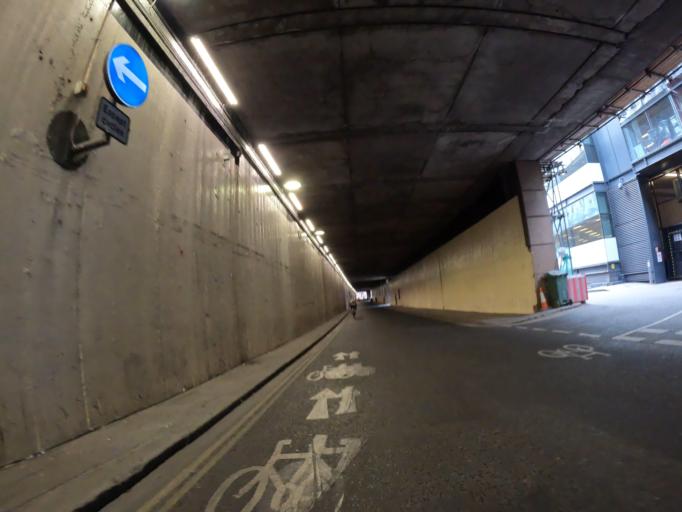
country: GB
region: England
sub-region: Greater London
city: Bethnal Green
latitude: 51.5436
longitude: -0.0784
